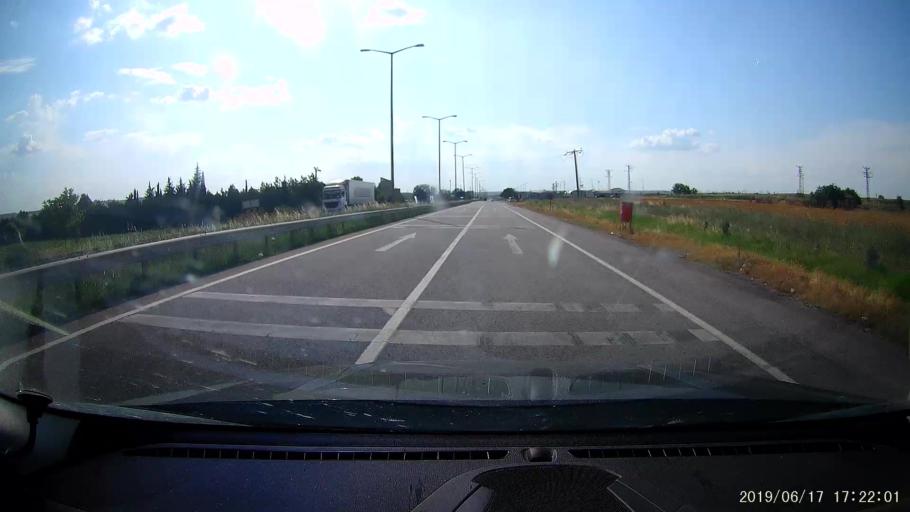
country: GR
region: East Macedonia and Thrace
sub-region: Nomos Evrou
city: Rizia
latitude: 41.7091
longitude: 26.3831
